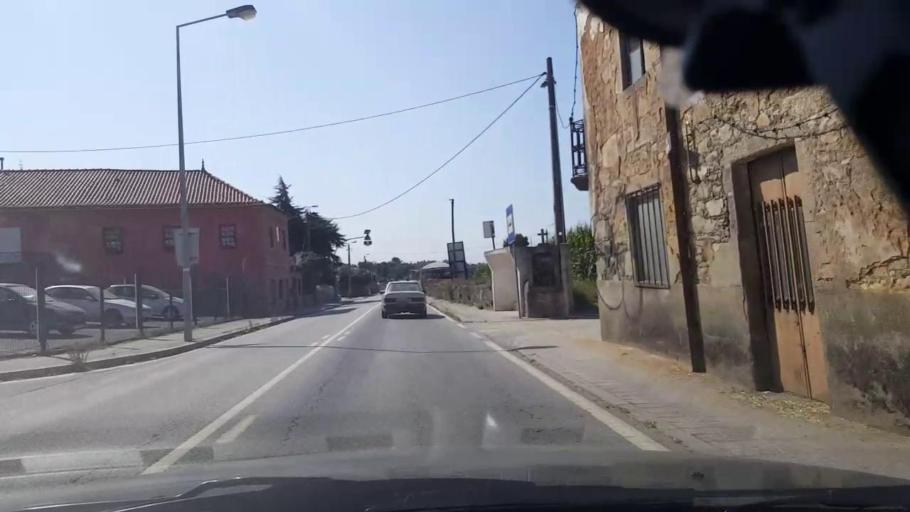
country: PT
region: Porto
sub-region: Povoa de Varzim
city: Pedroso
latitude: 41.4002
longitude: -8.6832
